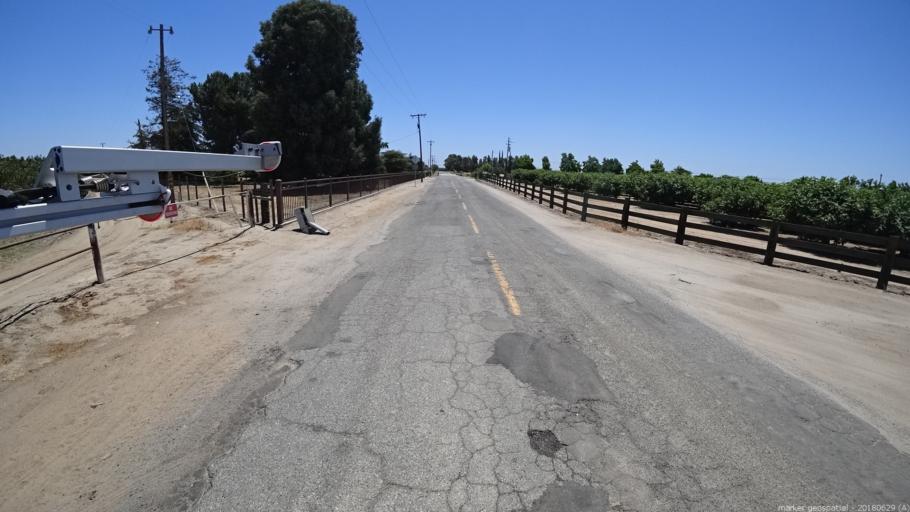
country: US
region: California
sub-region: Madera County
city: Parksdale
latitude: 36.9975
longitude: -120.0036
